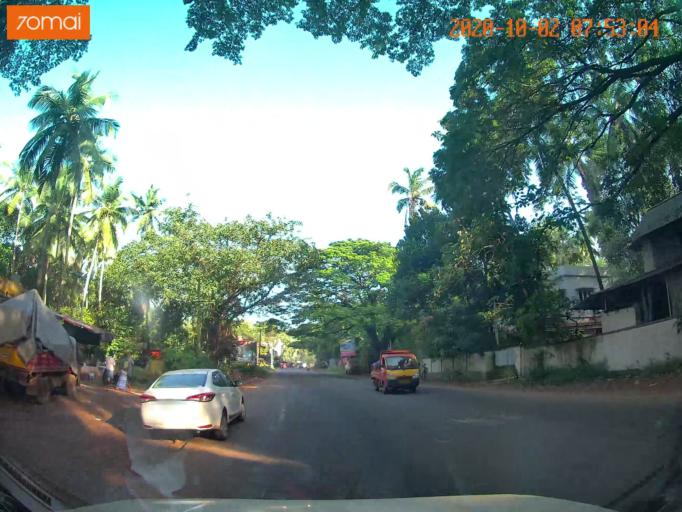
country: IN
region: Kerala
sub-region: Kozhikode
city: Ferokh
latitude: 11.1649
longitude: 75.8769
